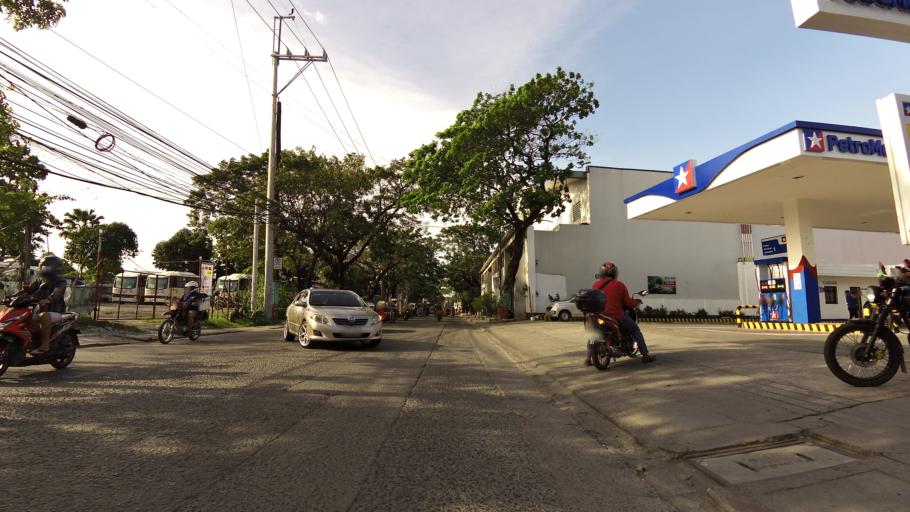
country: PH
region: Calabarzon
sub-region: Province of Rizal
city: Pateros
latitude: 14.5567
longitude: 121.0972
